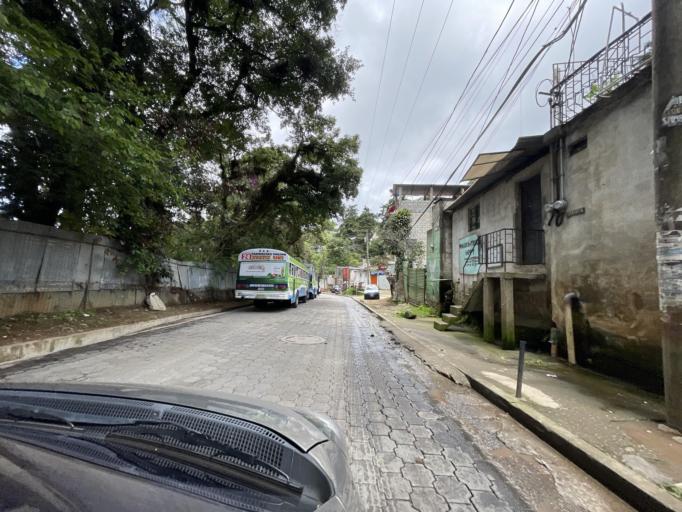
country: GT
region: Guatemala
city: Mixco
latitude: 14.6382
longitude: -90.6206
